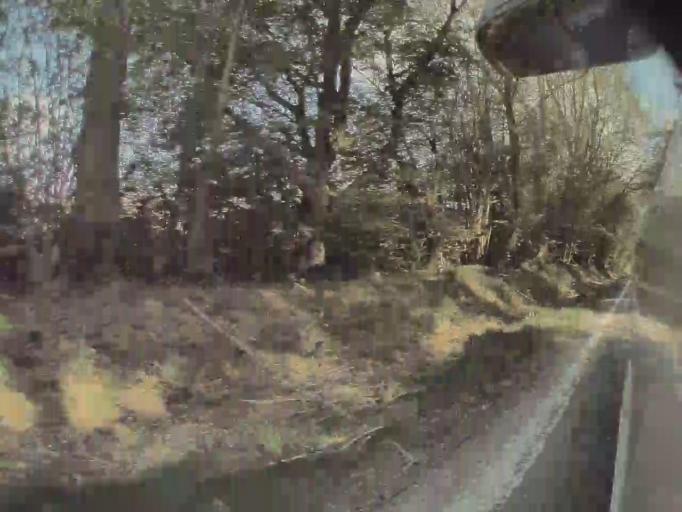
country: BE
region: Wallonia
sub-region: Province du Luxembourg
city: Tellin
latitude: 50.0338
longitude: 5.2073
